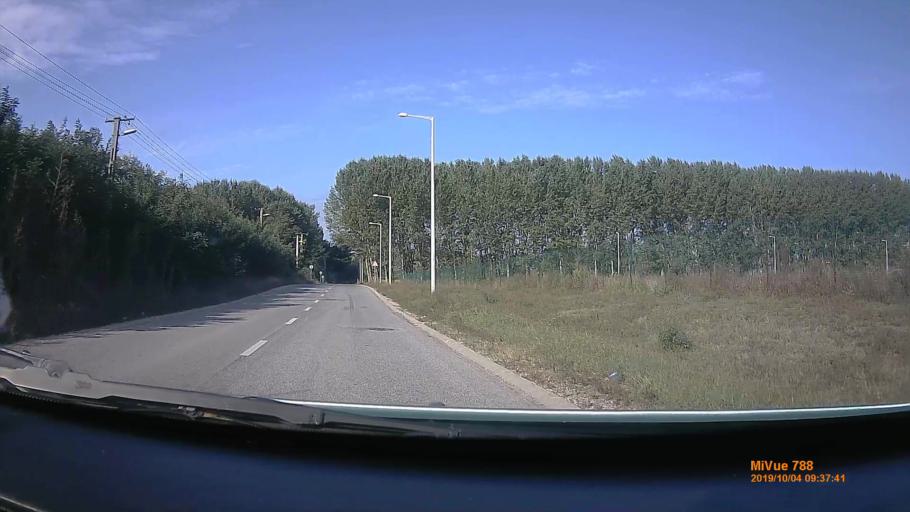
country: HU
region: Szabolcs-Szatmar-Bereg
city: Nyiregyhaza
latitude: 47.9447
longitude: 21.6477
